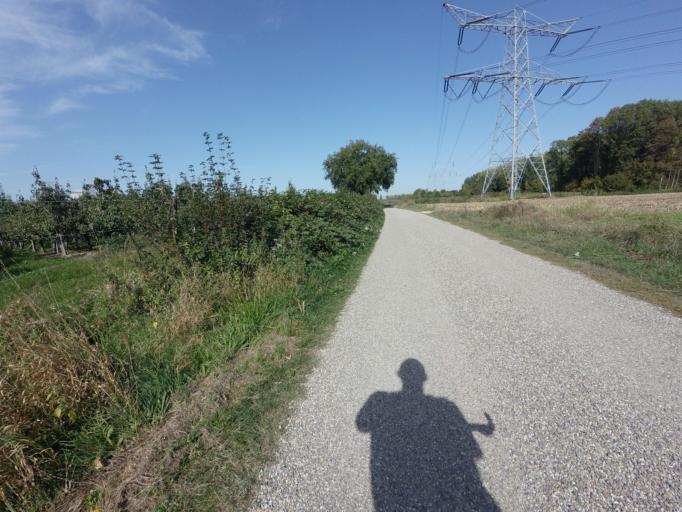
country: NL
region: Limburg
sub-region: Gemeente Maasgouw
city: Maasbracht
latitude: 51.1524
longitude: 5.9011
